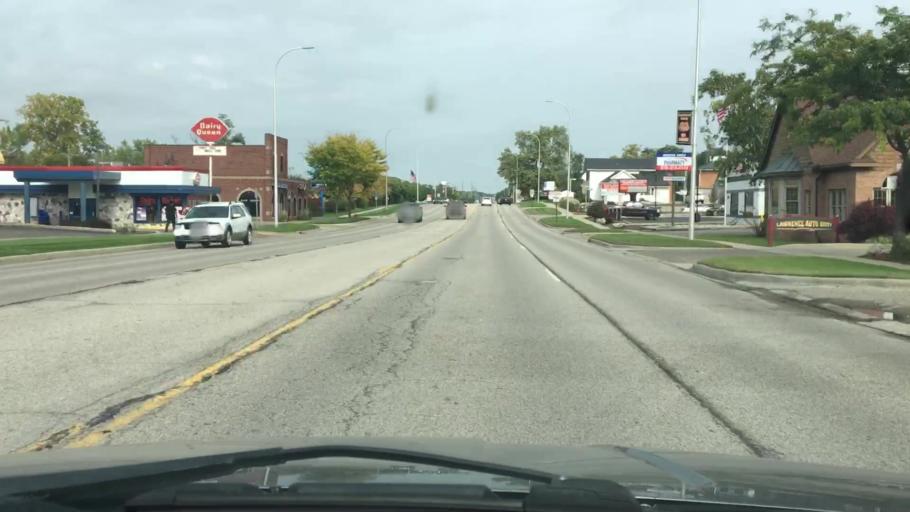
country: US
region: Michigan
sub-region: Livingston County
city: Brighton
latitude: 42.5312
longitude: -83.7812
